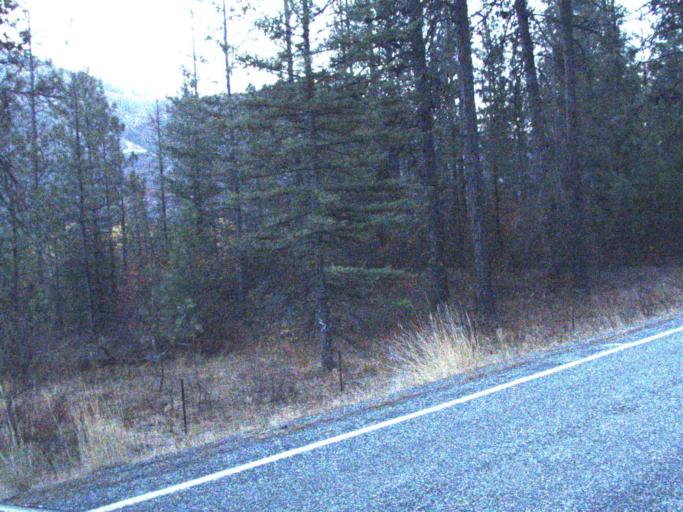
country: US
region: Washington
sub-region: Okanogan County
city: Coulee Dam
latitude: 48.2475
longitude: -118.6931
